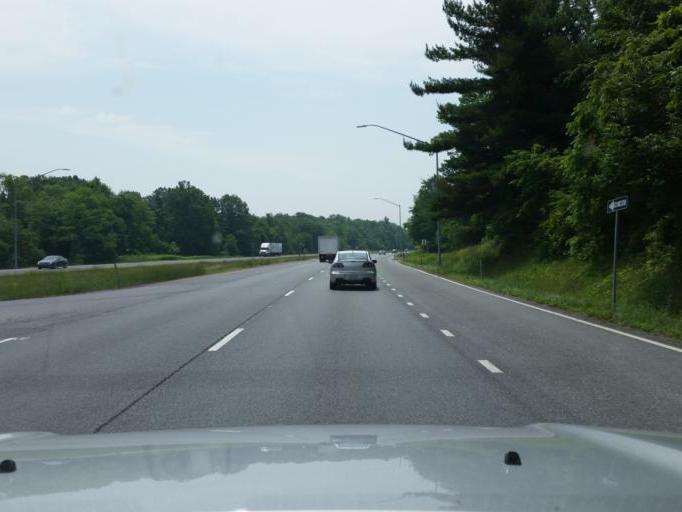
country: US
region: Maryland
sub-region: Frederick County
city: Walkersville
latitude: 39.5030
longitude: -77.4008
